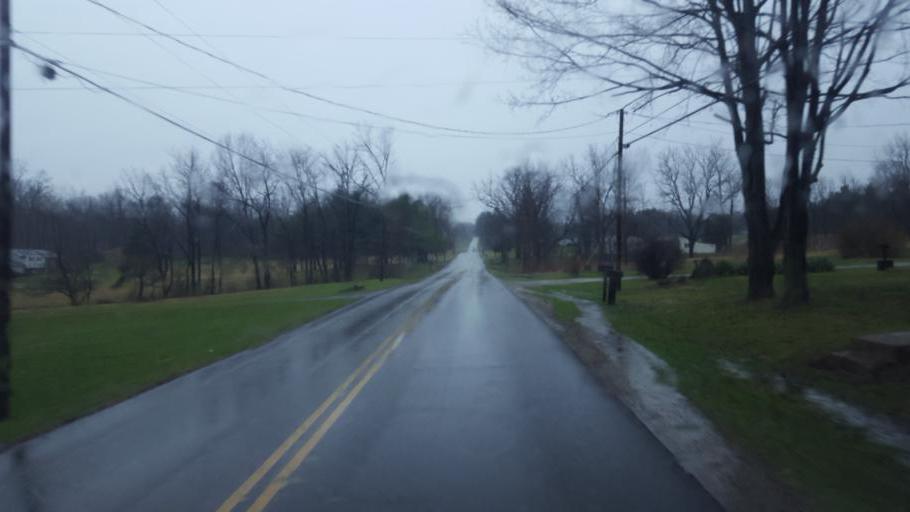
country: US
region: Ohio
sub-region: Knox County
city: Mount Vernon
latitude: 40.4207
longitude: -82.4883
